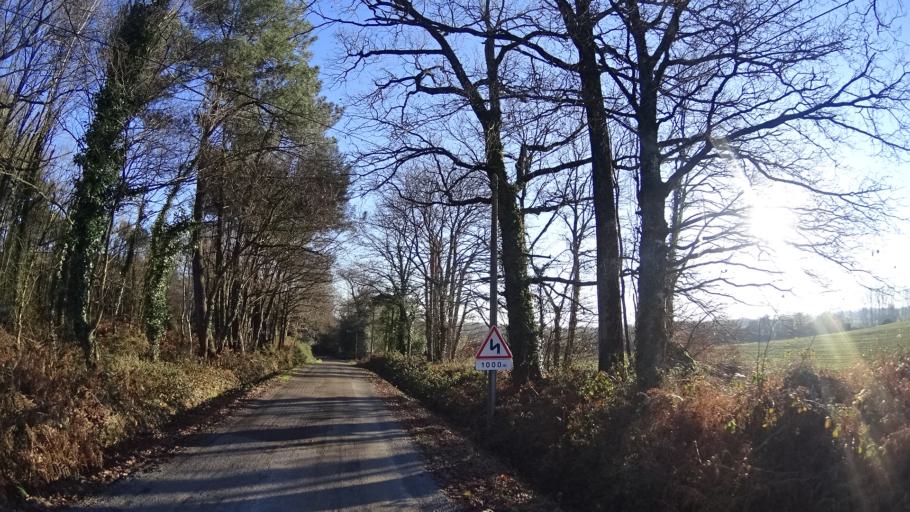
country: FR
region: Brittany
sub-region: Departement du Morbihan
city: Saint-Jacut-les-Pins
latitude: 47.6667
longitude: -2.1926
